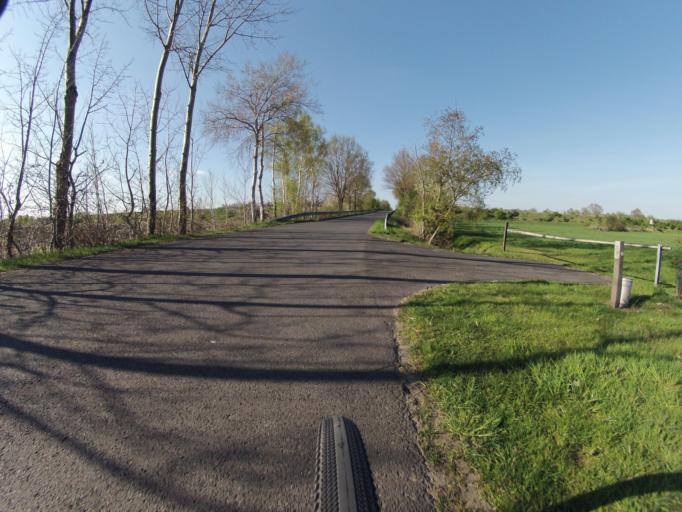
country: DE
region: Lower Saxony
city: Schuttorf
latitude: 52.3415
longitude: 7.2225
